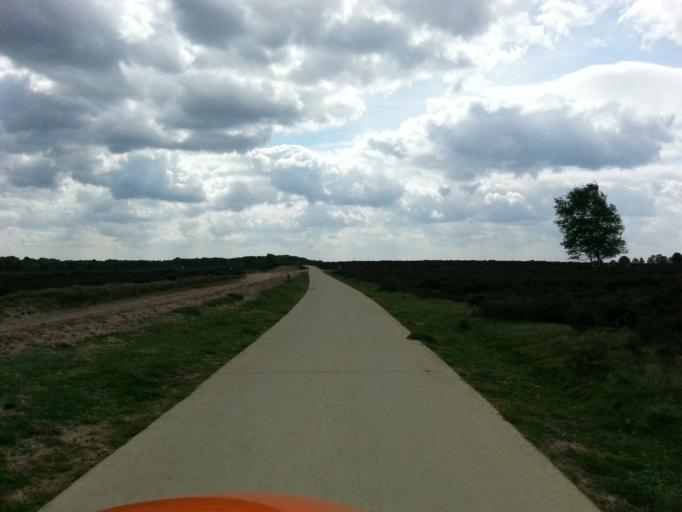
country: NL
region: Gelderland
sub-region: Gemeente Ede
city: Ede
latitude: 52.0441
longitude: 5.7145
